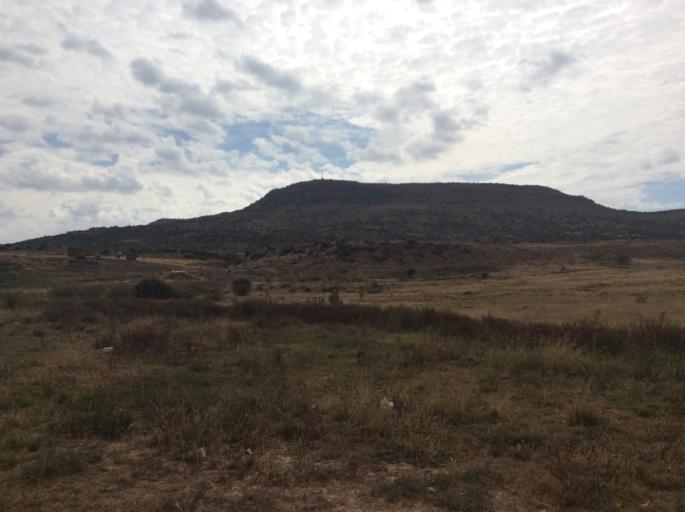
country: LS
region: Mafeteng
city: Mafeteng
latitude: -29.7181
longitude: 27.0225
